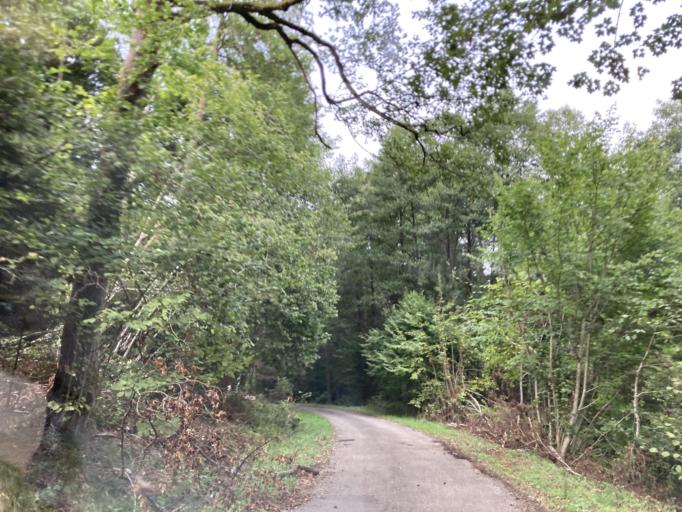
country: DE
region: Baden-Wuerttemberg
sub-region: Karlsruhe Region
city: Dobel
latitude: 48.7689
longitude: 8.4939
